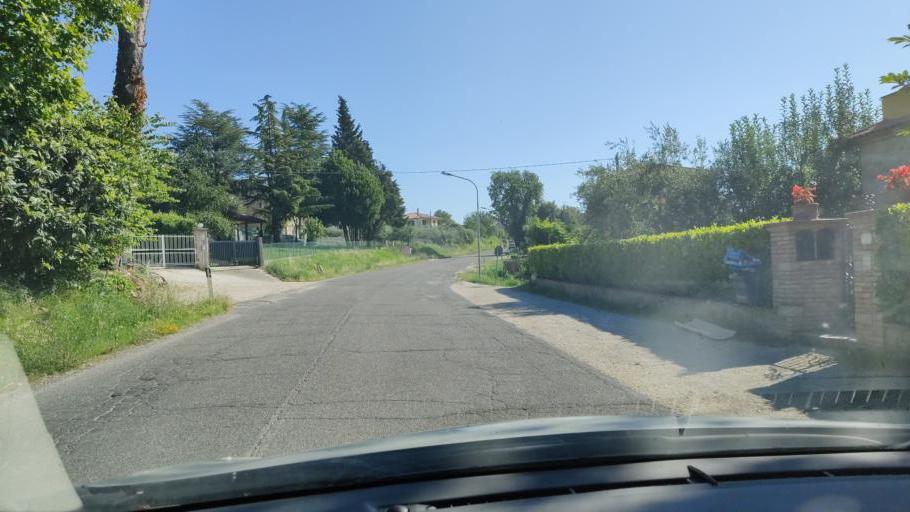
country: IT
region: Umbria
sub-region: Provincia di Terni
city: Avigliano Umbro
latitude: 42.6524
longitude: 12.4209
